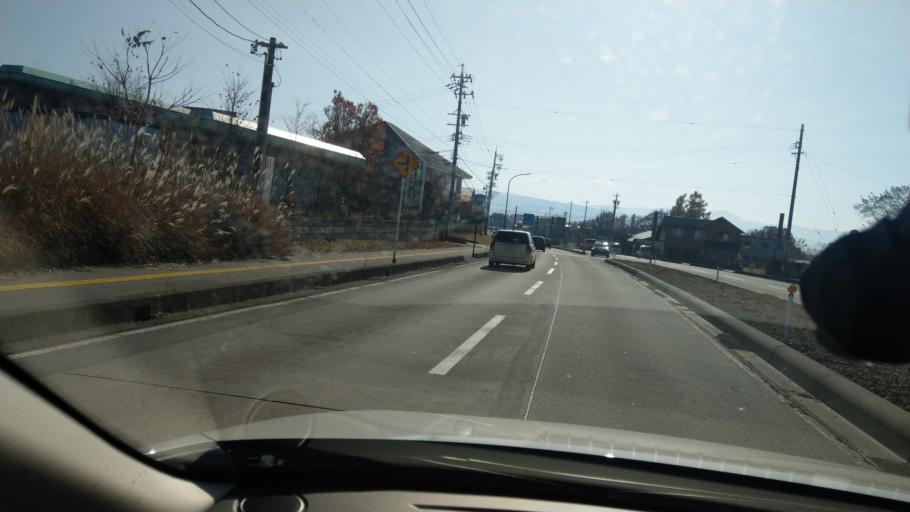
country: JP
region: Nagano
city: Komoro
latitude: 36.2910
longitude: 138.4712
